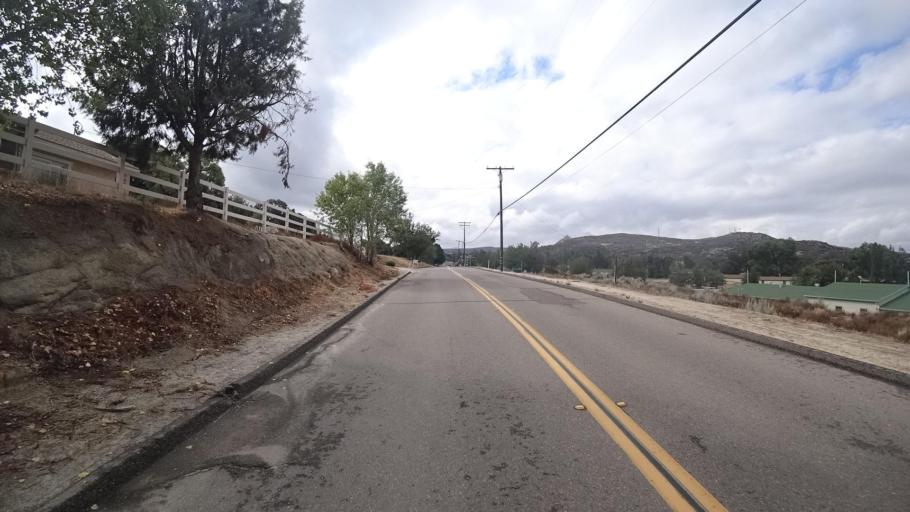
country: US
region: California
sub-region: San Diego County
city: Campo
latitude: 32.6105
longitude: -116.4698
